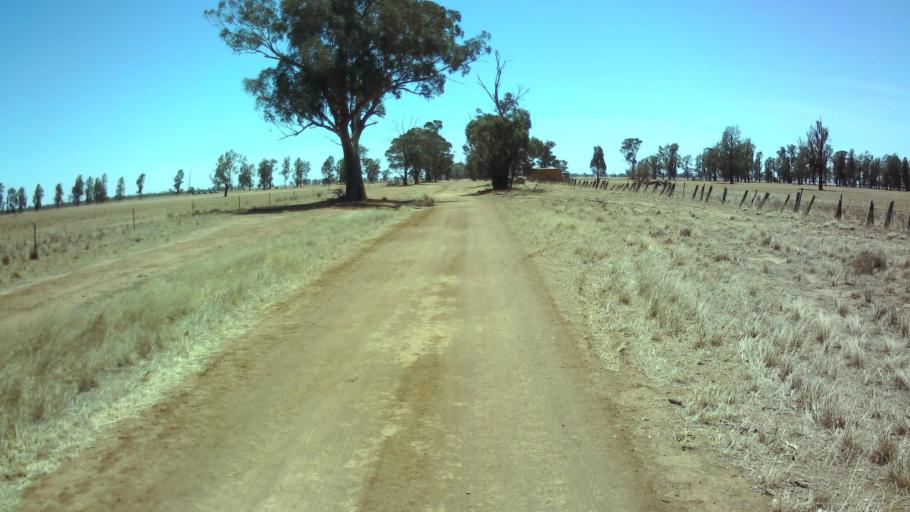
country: AU
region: New South Wales
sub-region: Weddin
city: Grenfell
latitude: -33.9710
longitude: 147.7381
